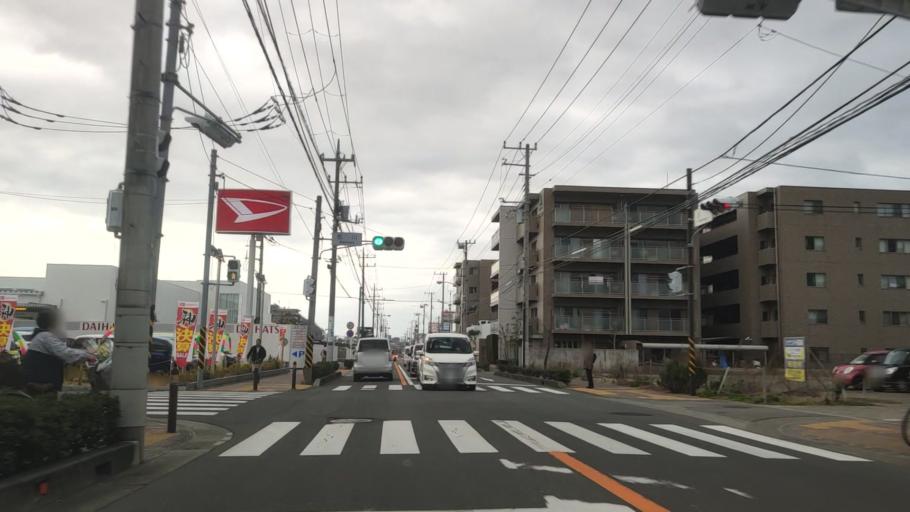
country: JP
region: Kanagawa
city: Odawara
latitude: 35.2799
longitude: 139.1950
